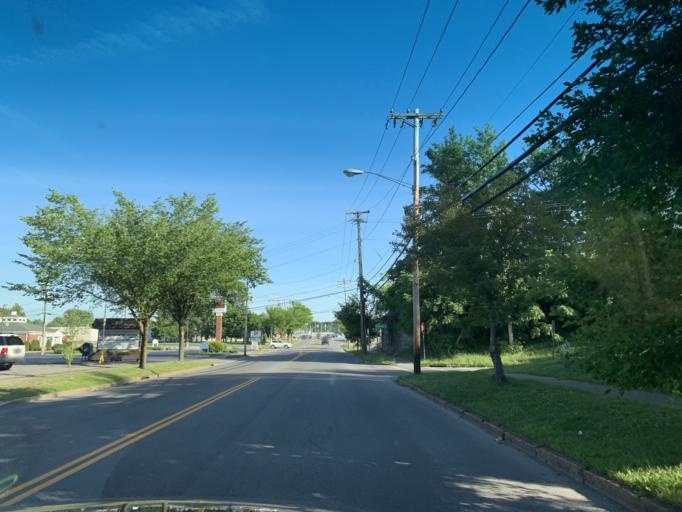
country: US
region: New York
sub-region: Madison County
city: Oneida
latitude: 43.0808
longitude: -75.6433
